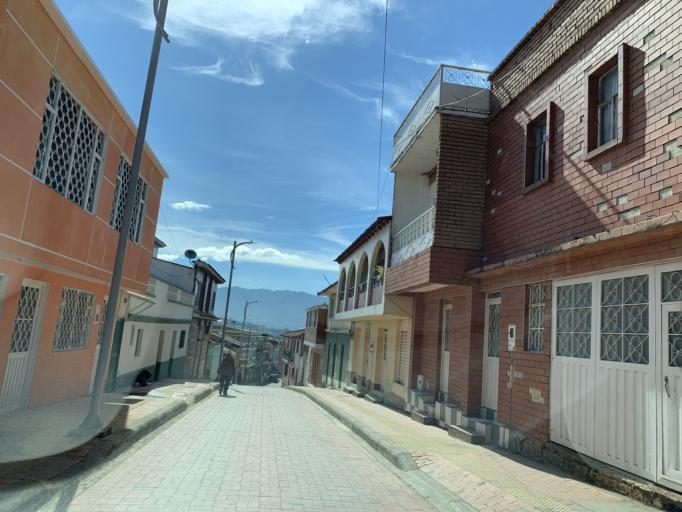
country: CO
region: Boyaca
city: Santa Sofia
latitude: 5.7139
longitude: -73.6034
